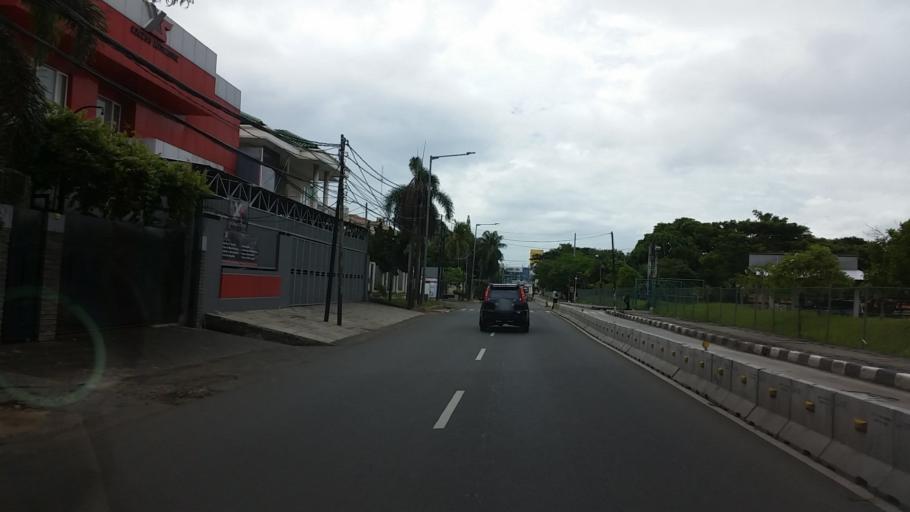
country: ID
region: Jakarta Raya
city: Jakarta
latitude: -6.1178
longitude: 106.7880
